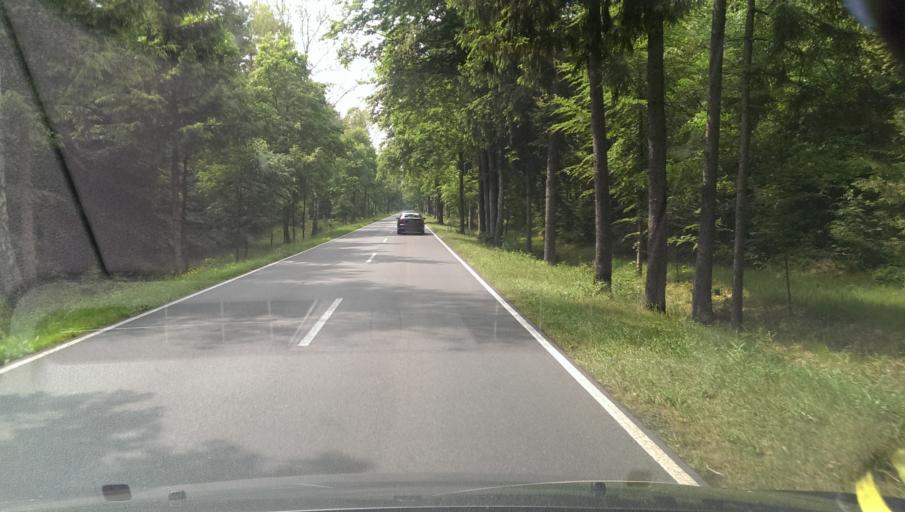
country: DE
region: Lower Saxony
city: Sprakensehl
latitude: 52.7859
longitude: 10.4045
